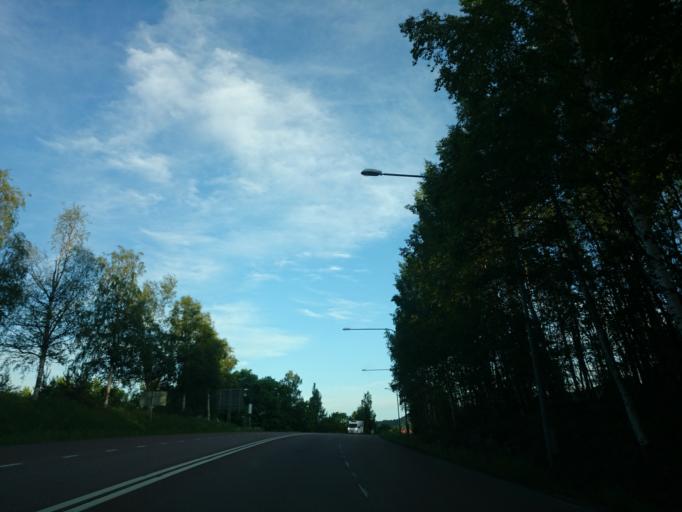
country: SE
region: Vaesternorrland
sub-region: Sundsvalls Kommun
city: Stockvik
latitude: 62.3280
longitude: 17.3688
